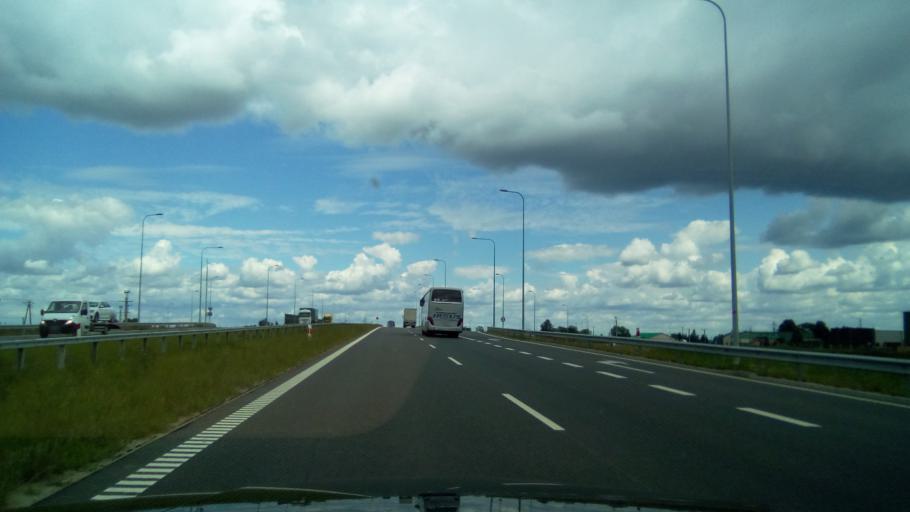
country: PL
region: Kujawsko-Pomorskie
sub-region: Powiat zninski
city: Znin
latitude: 52.8473
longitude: 17.6925
